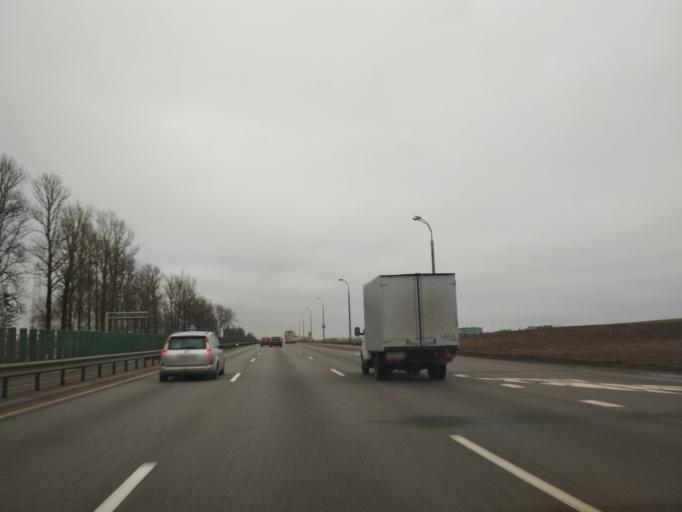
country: BY
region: Minsk
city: Yubilyeyny
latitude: 53.8379
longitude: 27.5078
